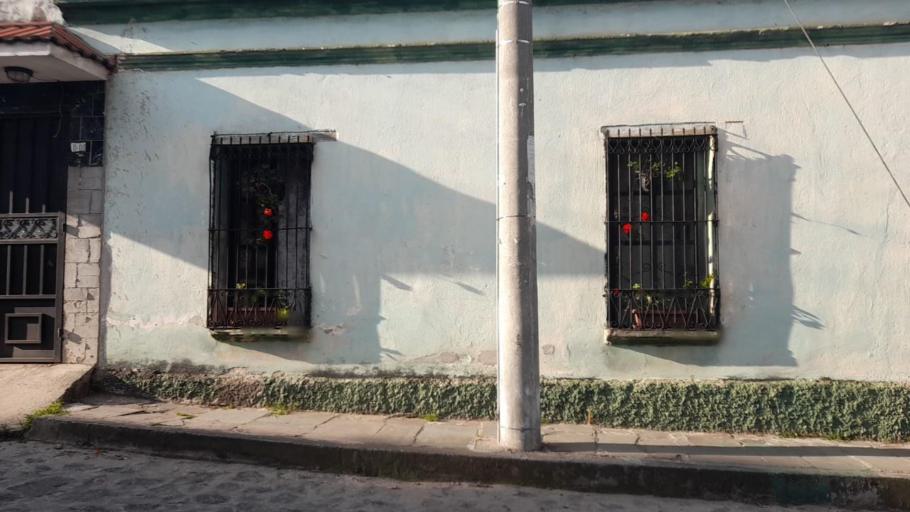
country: GT
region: Quetzaltenango
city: Quetzaltenango
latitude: 14.8386
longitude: -91.5118
